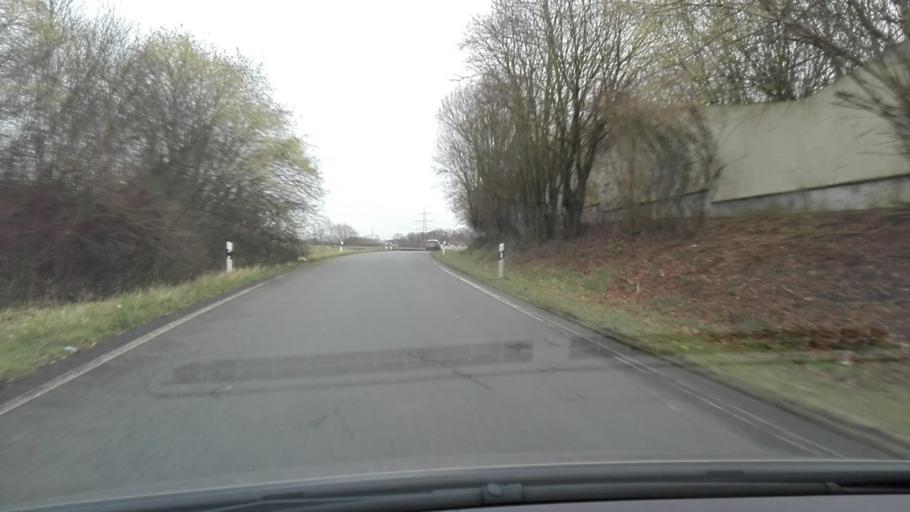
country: DE
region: North Rhine-Westphalia
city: Lanstrop
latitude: 51.5347
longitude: 7.5478
